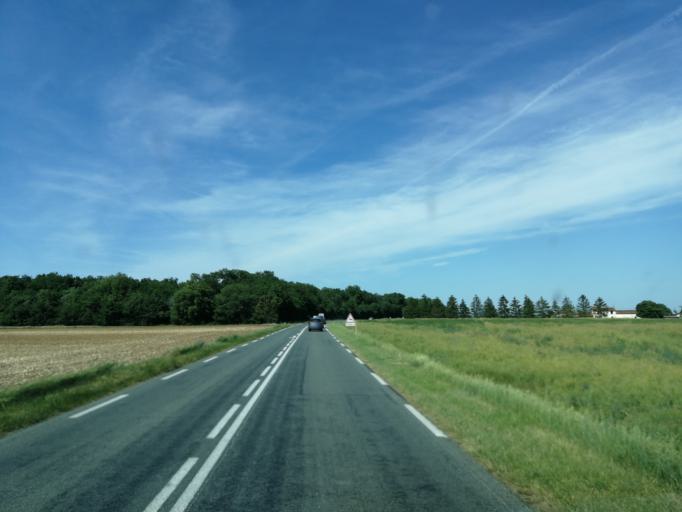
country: FR
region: Poitou-Charentes
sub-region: Departement de la Vienne
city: Loudun
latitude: 47.0395
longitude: 0.1269
